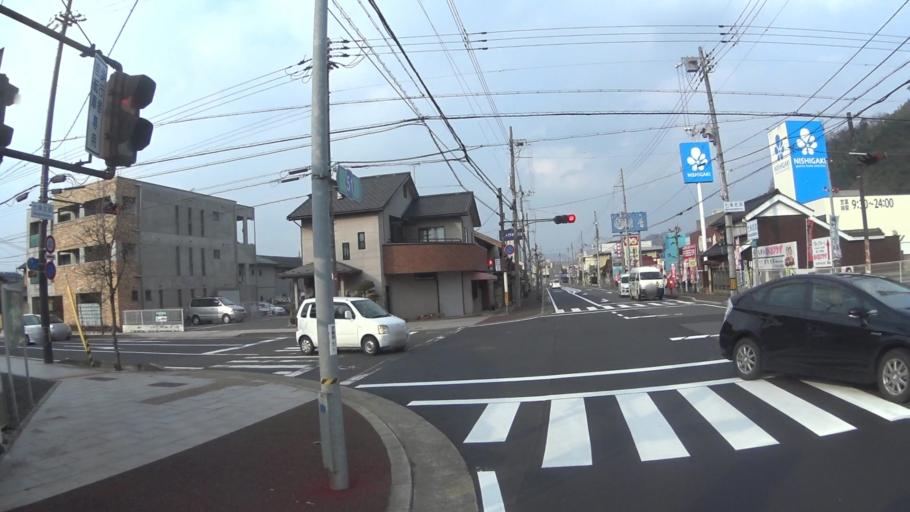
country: JP
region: Kyoto
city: Maizuru
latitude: 35.4676
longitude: 135.3973
